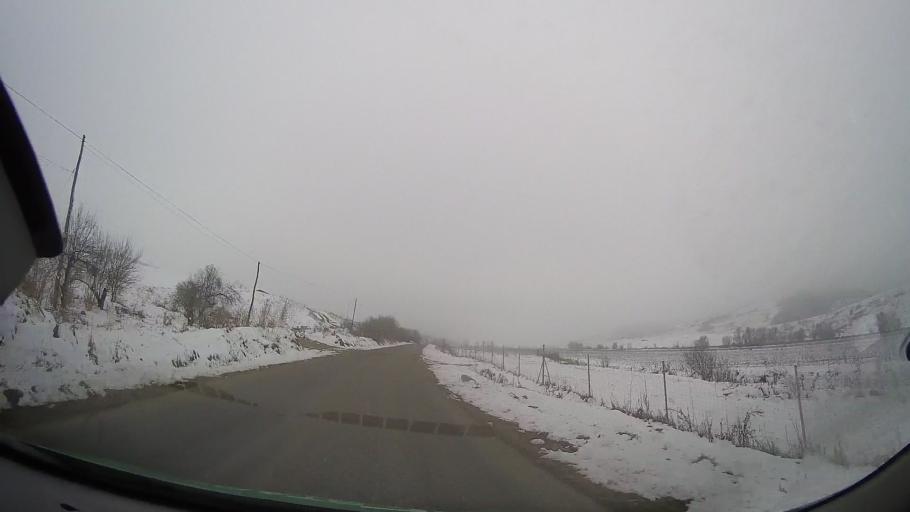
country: RO
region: Bacau
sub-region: Comuna Vultureni
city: Vultureni
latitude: 46.3653
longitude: 27.2856
